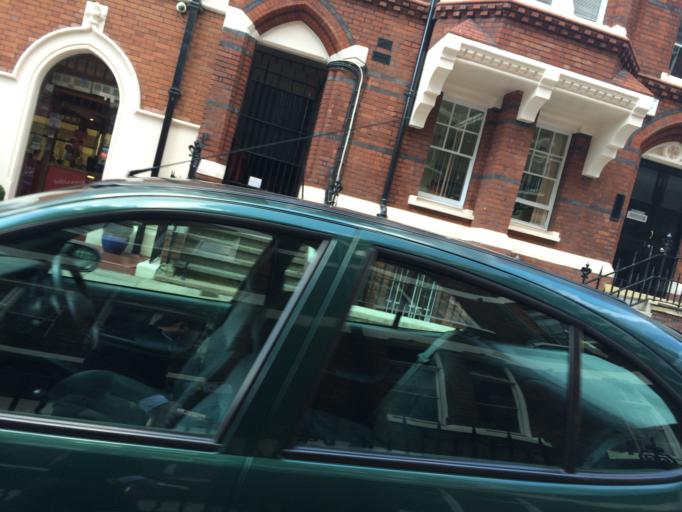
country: GB
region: England
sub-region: Greater London
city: London
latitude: 51.5133
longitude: -0.1522
